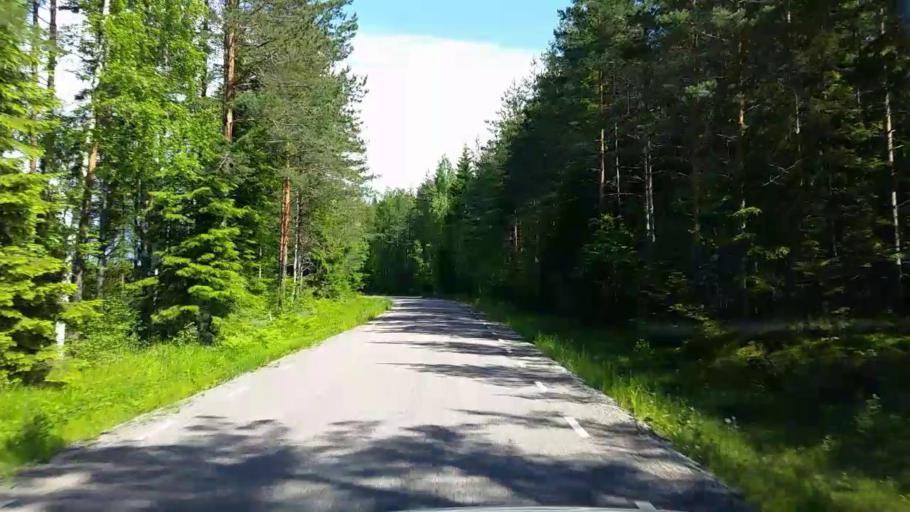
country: SE
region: Vaestmanland
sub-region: Fagersta Kommun
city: Fagersta
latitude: 59.9874
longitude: 15.7411
